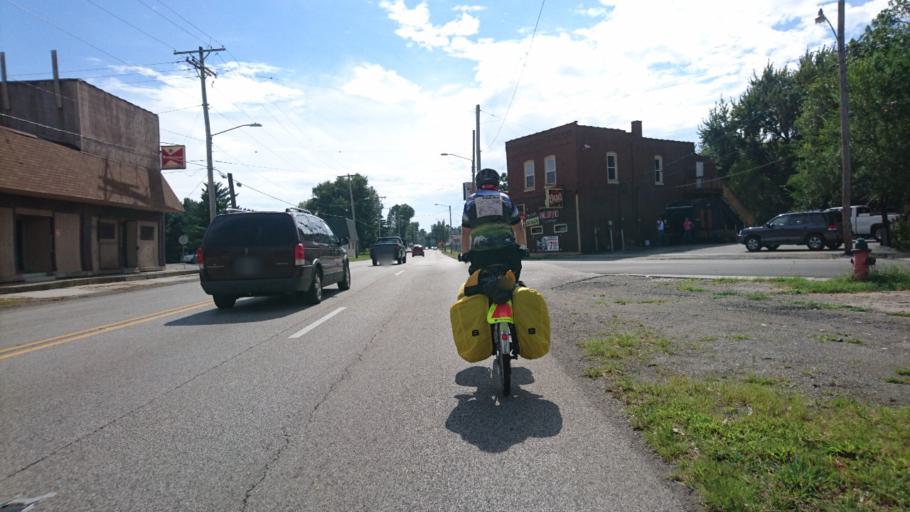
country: US
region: Illinois
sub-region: Sangamon County
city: Grandview
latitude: 39.8274
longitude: -89.6396
